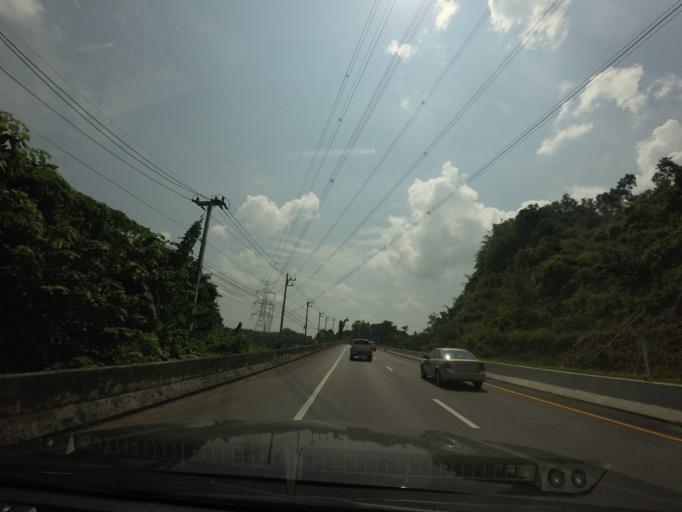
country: TH
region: Uttaradit
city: Uttaradit
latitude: 17.7685
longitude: 100.1323
